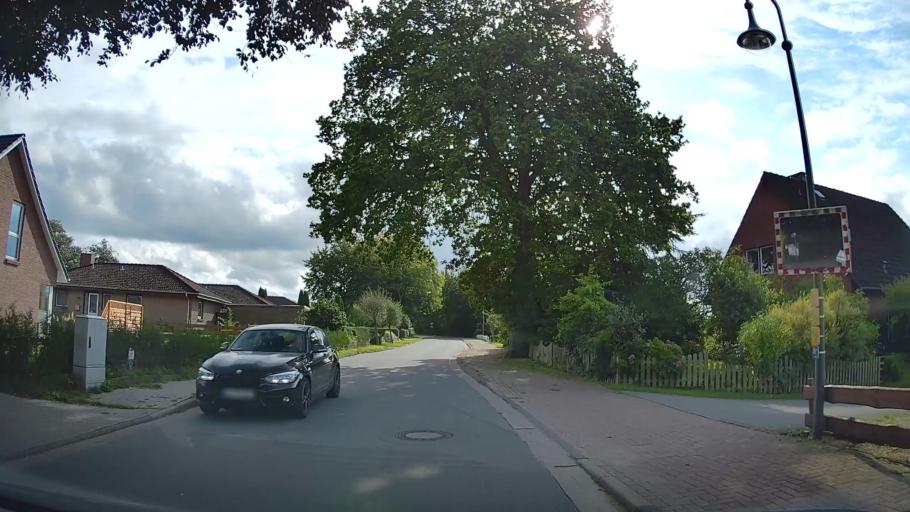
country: DE
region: Schleswig-Holstein
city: Ringsberg
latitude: 54.8055
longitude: 9.5984
